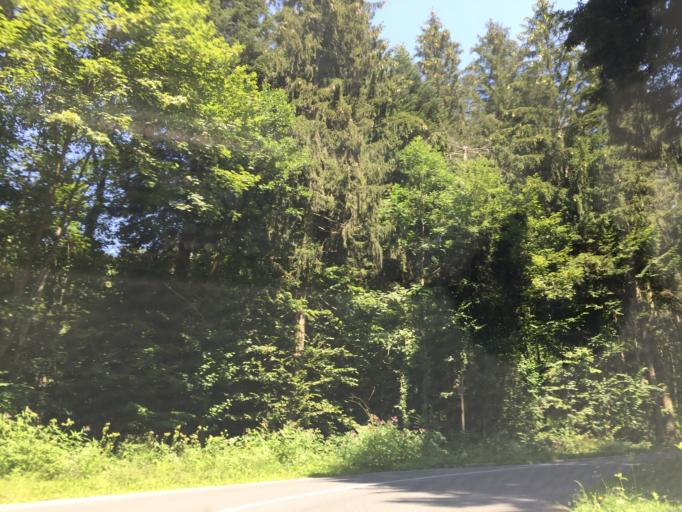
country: SI
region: Trbovlje
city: Trbovlje
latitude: 46.1851
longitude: 15.0596
